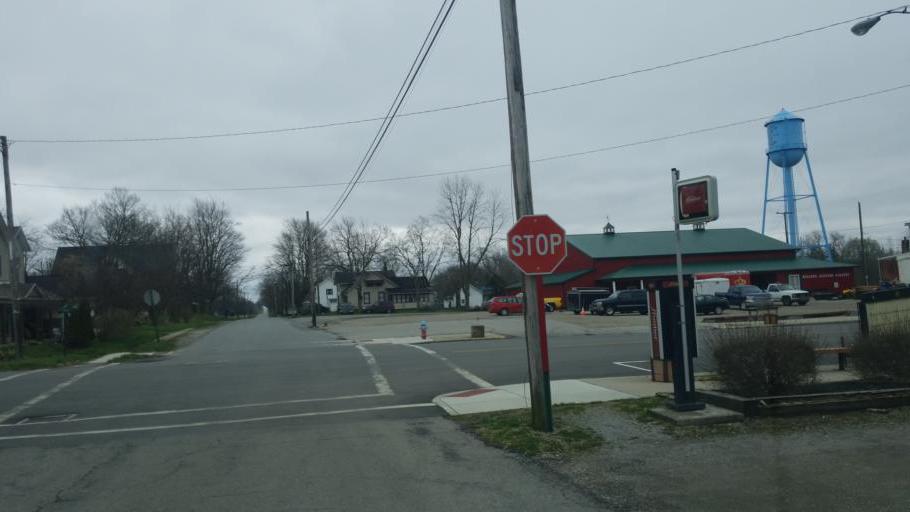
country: US
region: Ohio
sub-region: Wyandot County
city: Upper Sandusky
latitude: 40.8190
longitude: -83.1310
